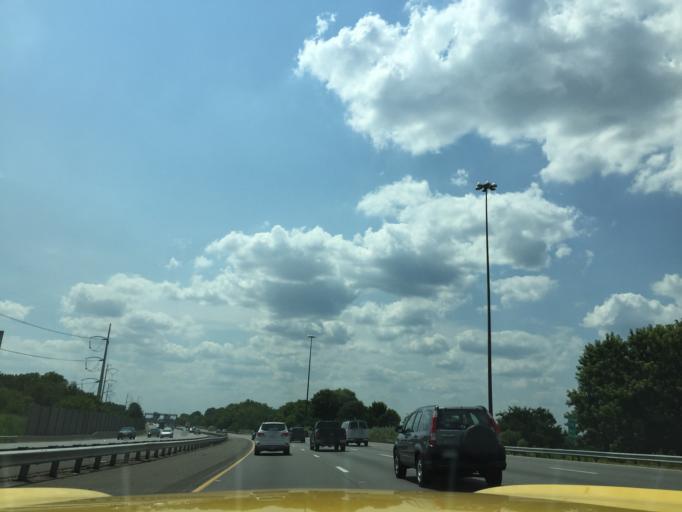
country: US
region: Pennsylvania
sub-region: Delaware County
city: Folcroft
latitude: 39.8763
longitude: -75.2834
